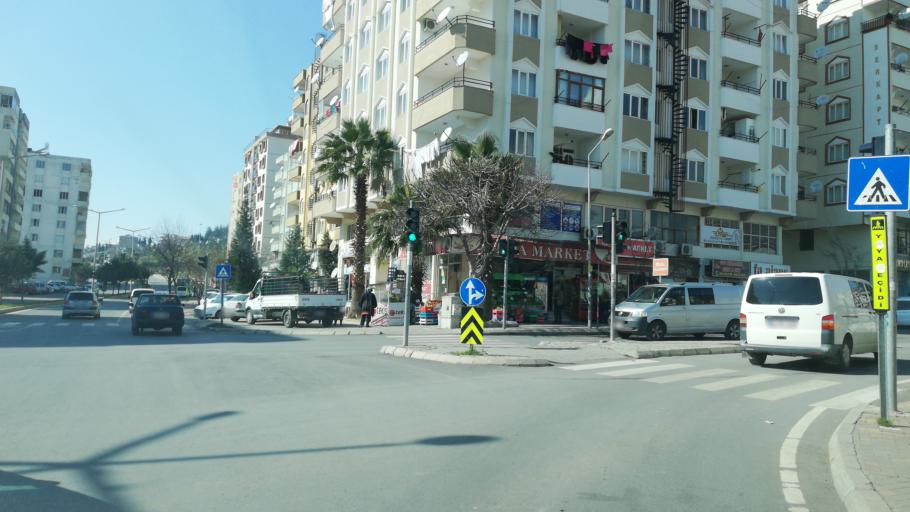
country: TR
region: Kahramanmaras
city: Kahramanmaras
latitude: 37.5716
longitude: 36.9201
